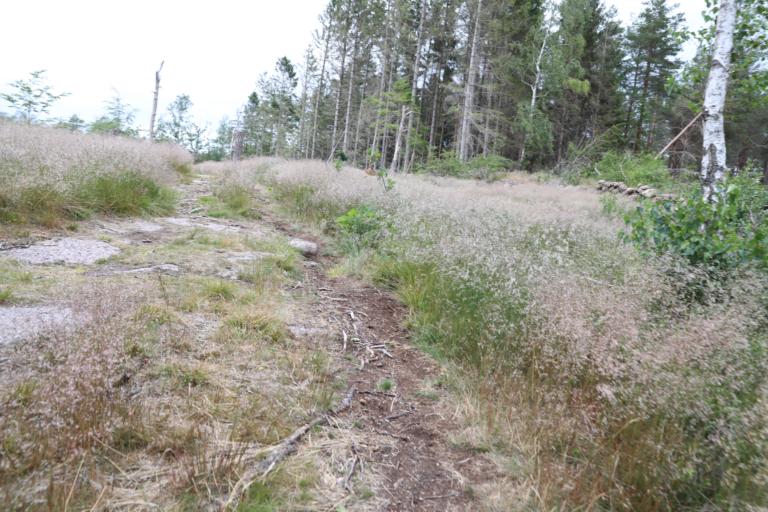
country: SE
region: Halland
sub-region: Varbergs Kommun
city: Varberg
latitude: 57.1680
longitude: 12.2618
